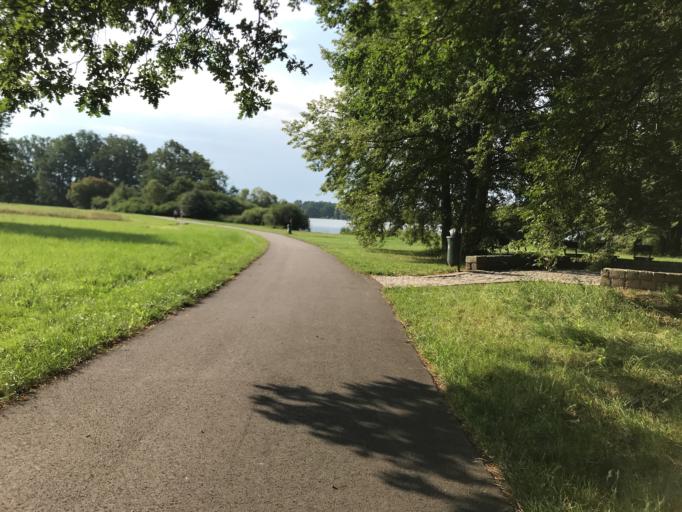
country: CZ
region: Jihocesky
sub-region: Okres Jindrichuv Hradec
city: Trebon
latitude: 48.9985
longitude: 14.7480
